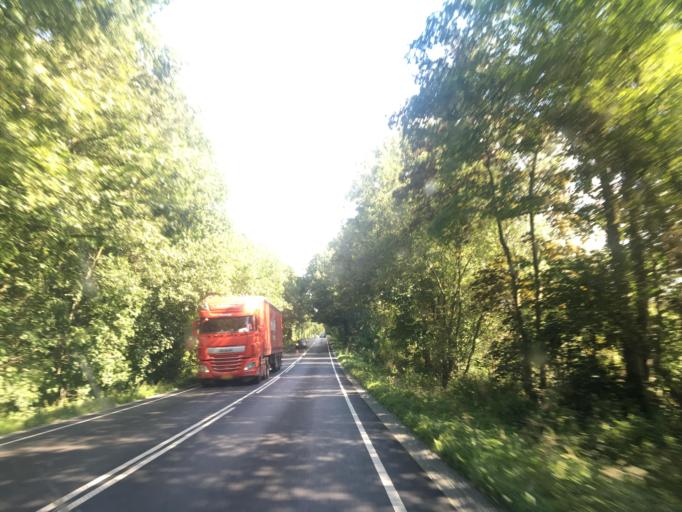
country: DK
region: South Denmark
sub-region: Middelfart Kommune
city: Ejby
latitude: 55.4022
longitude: 9.8934
